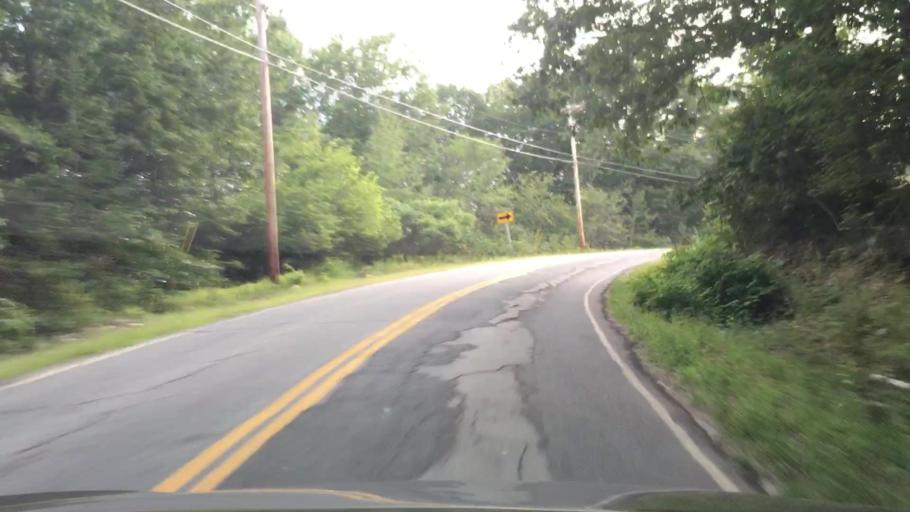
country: US
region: Maine
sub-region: Hancock County
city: Penobscot
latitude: 44.4725
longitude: -68.7297
